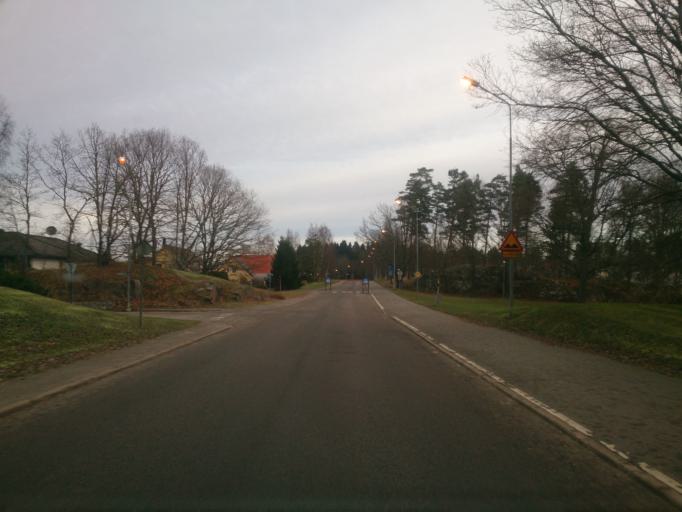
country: SE
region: OEstergoetland
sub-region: Atvidabergs Kommun
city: Atvidaberg
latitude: 58.1987
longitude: 15.9844
